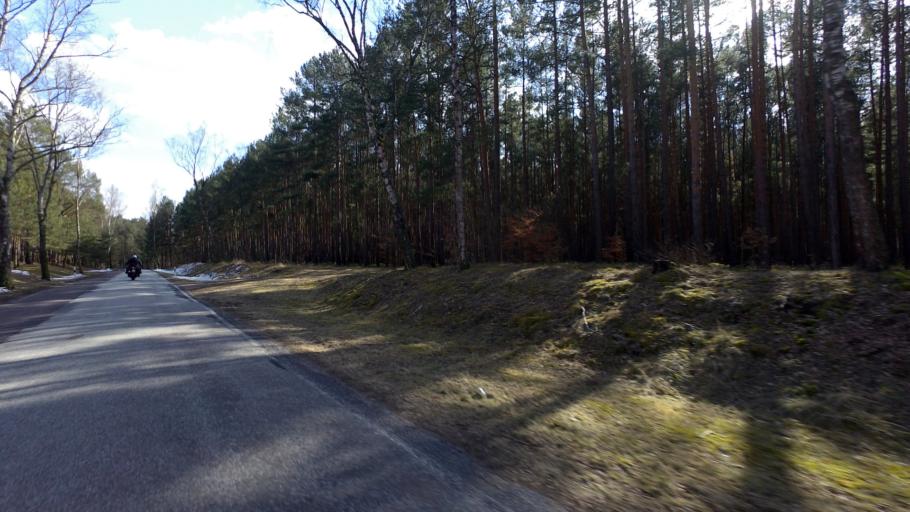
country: DE
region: Brandenburg
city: Biesenthal
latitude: 52.7807
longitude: 13.6128
